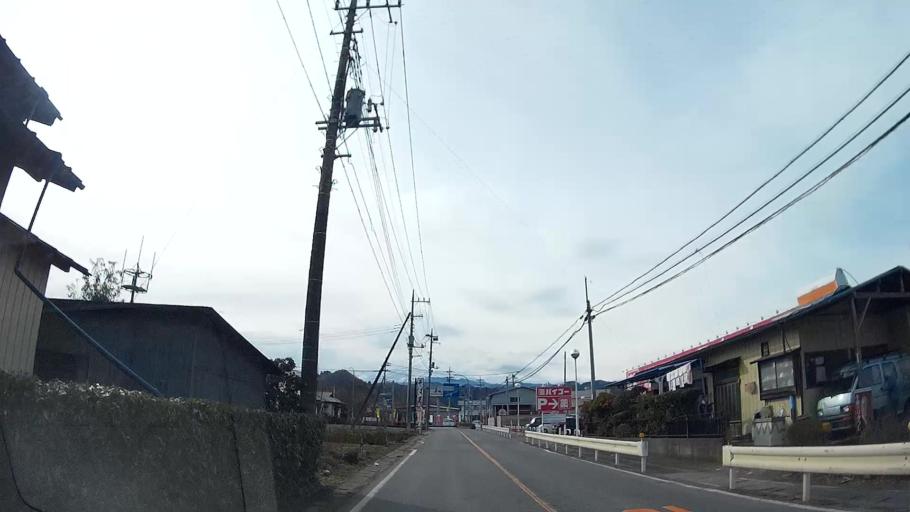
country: JP
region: Saitama
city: Chichibu
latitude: 36.0155
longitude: 139.0356
